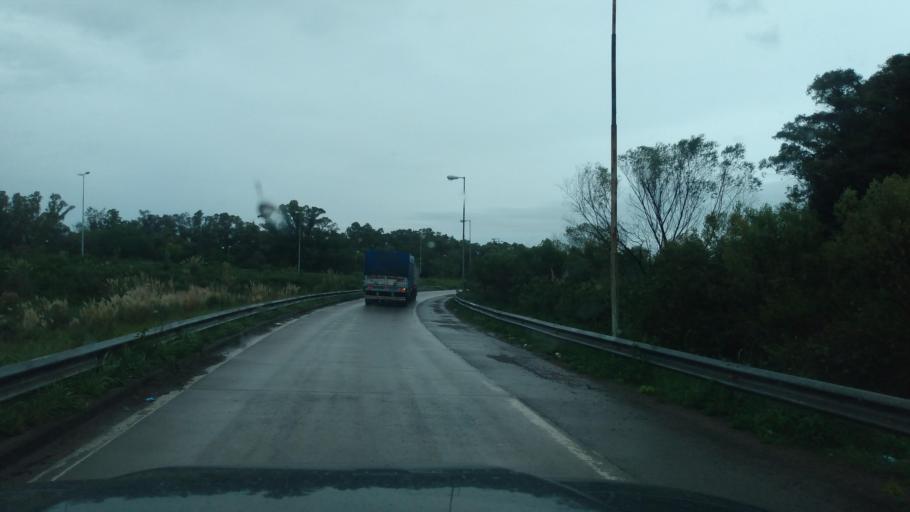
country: AR
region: Buenos Aires
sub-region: Partido de Pilar
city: Pilar
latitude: -34.3958
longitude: -59.0244
